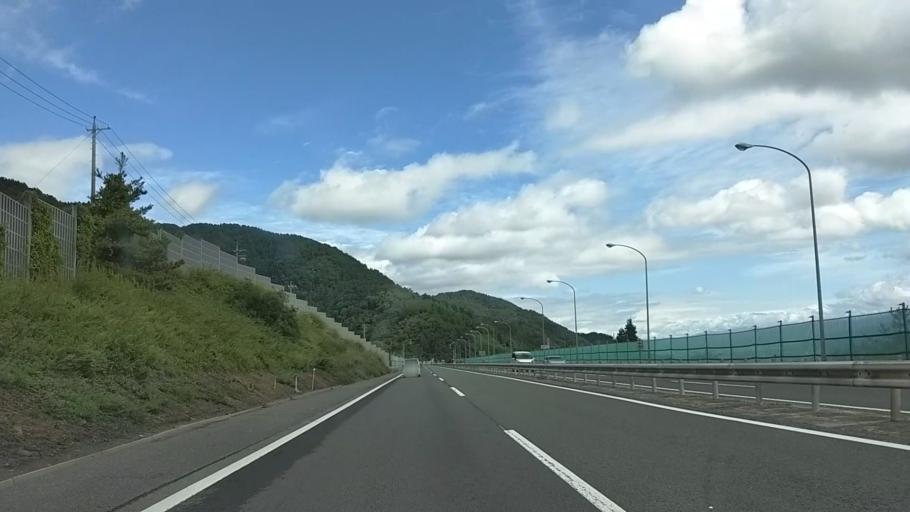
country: JP
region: Nagano
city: Nagano-shi
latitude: 36.5220
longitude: 138.0762
